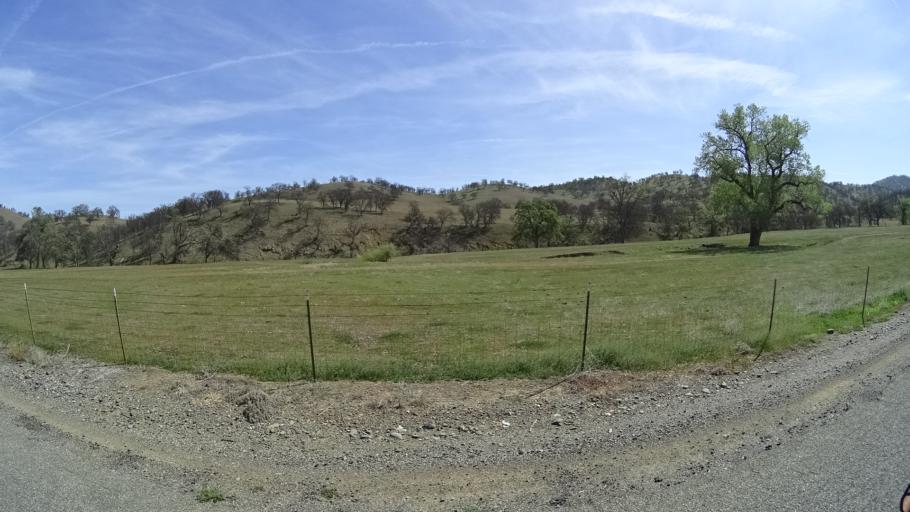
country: US
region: California
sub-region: Glenn County
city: Willows
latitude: 39.5160
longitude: -122.4569
